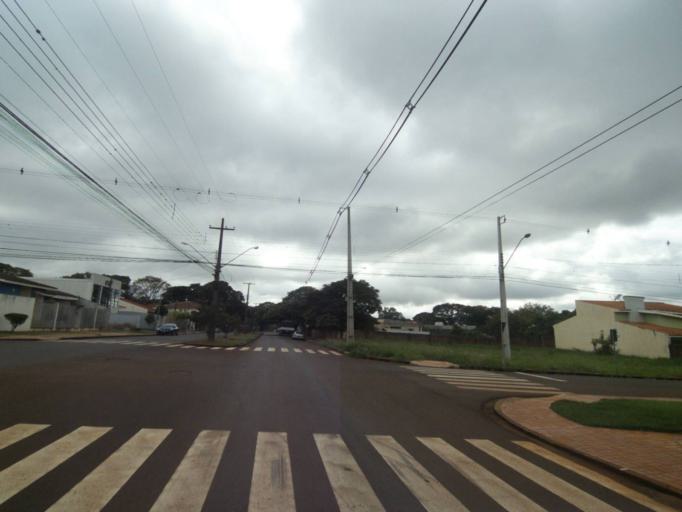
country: BR
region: Parana
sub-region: Campo Mourao
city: Campo Mourao
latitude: -24.0440
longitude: -52.3703
